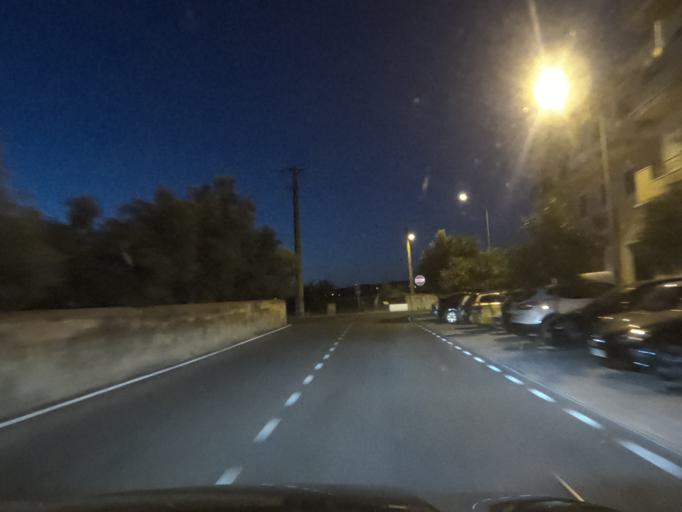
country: PT
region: Faro
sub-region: Loule
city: Loule
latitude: 37.1383
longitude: -8.0078
